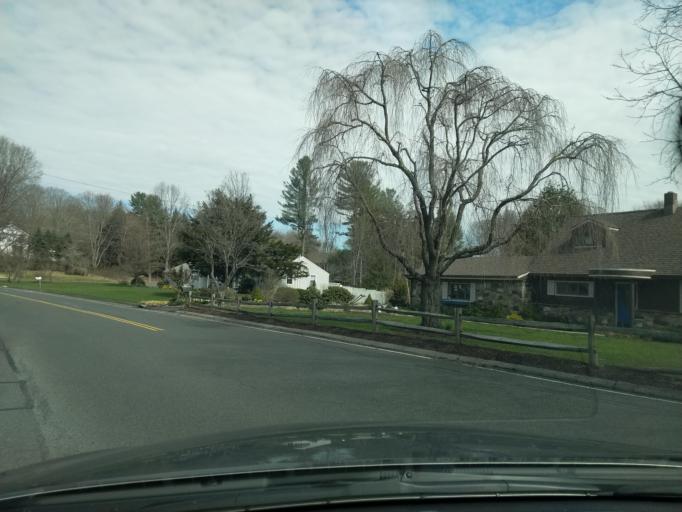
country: US
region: Connecticut
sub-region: Fairfield County
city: Trumbull
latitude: 41.3433
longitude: -73.2252
